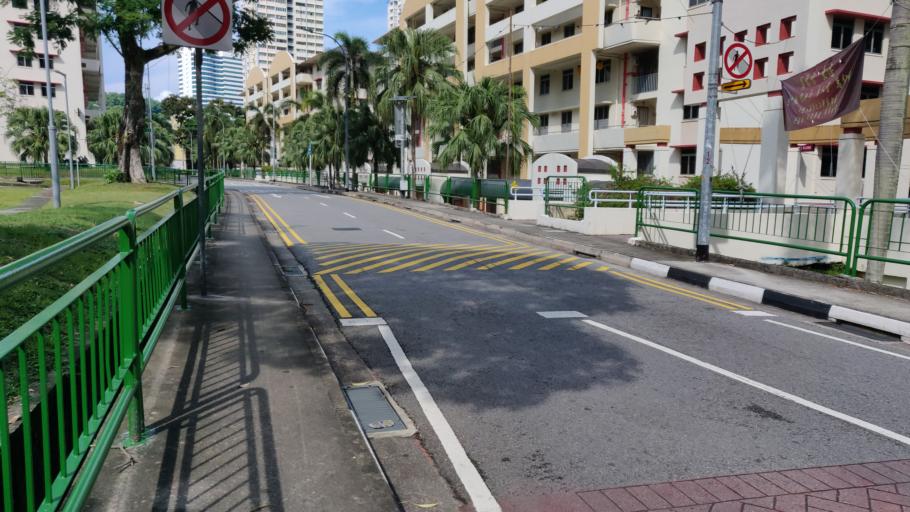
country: SG
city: Singapore
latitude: 1.2859
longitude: 103.8166
